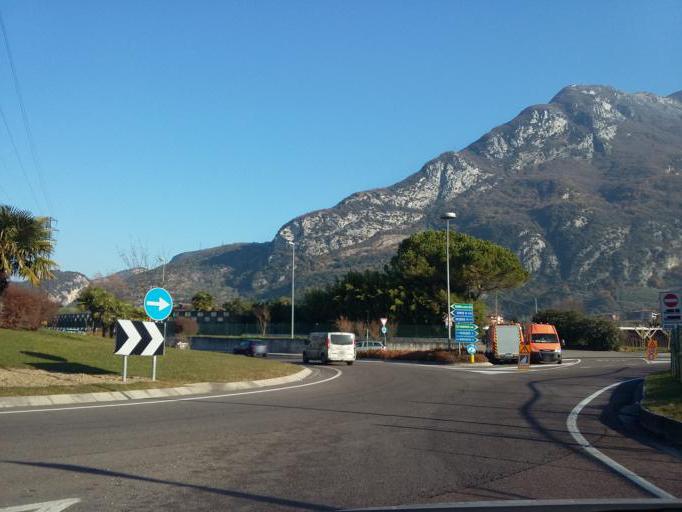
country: IT
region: Trentino-Alto Adige
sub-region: Provincia di Trento
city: Arco
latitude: 45.9140
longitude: 10.8949
